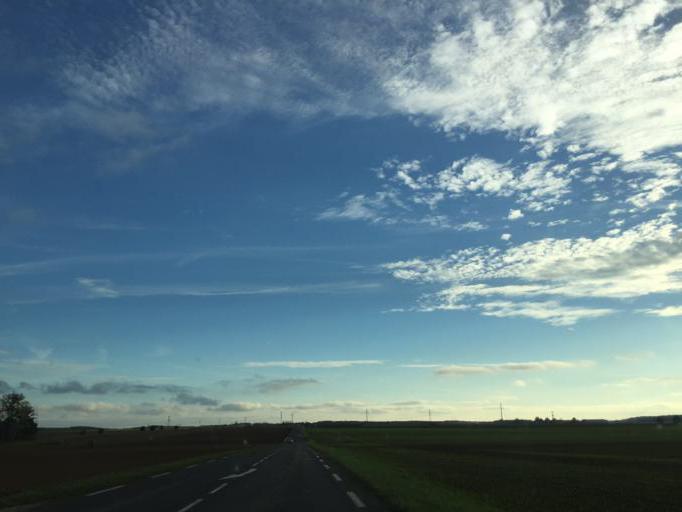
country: FR
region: Ile-de-France
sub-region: Departement de Seine-et-Marne
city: Jouy-le-Chatel
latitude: 48.6247
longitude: 3.1024
